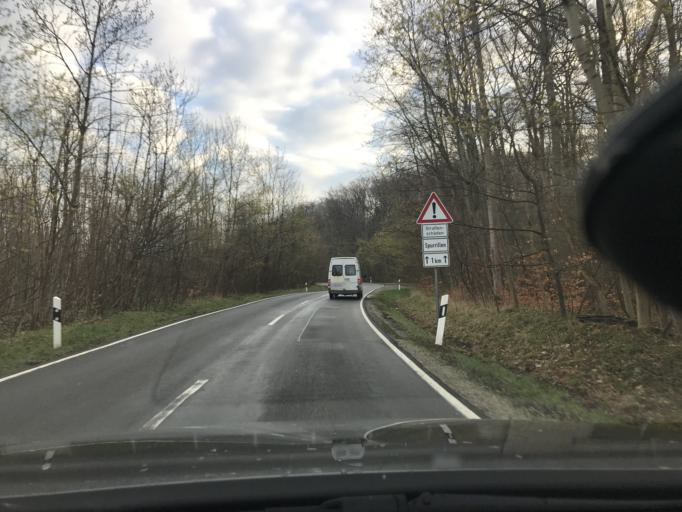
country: DE
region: Thuringia
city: Menteroda
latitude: 51.2941
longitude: 10.5521
